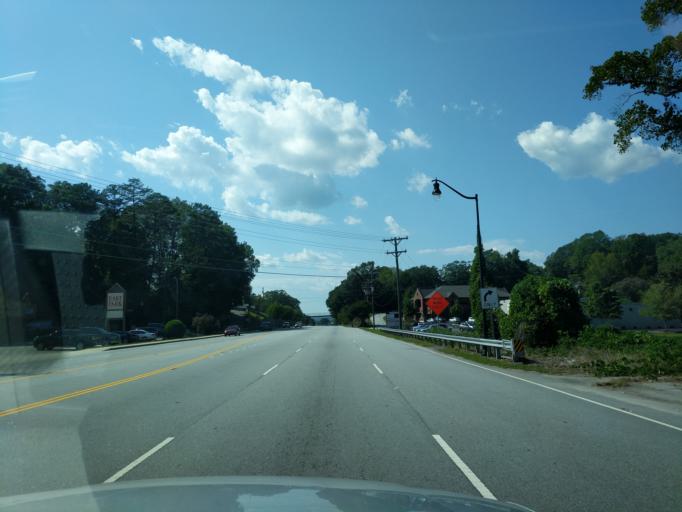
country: US
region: South Carolina
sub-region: Pickens County
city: Clemson
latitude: 34.6878
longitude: -82.8192
